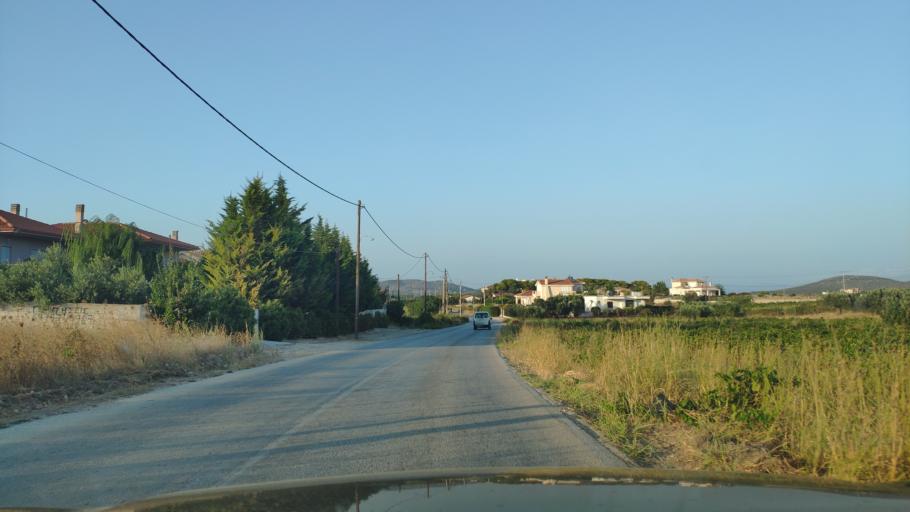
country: GR
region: Attica
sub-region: Nomarchia Anatolikis Attikis
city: Markopoulo
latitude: 37.9020
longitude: 23.9589
